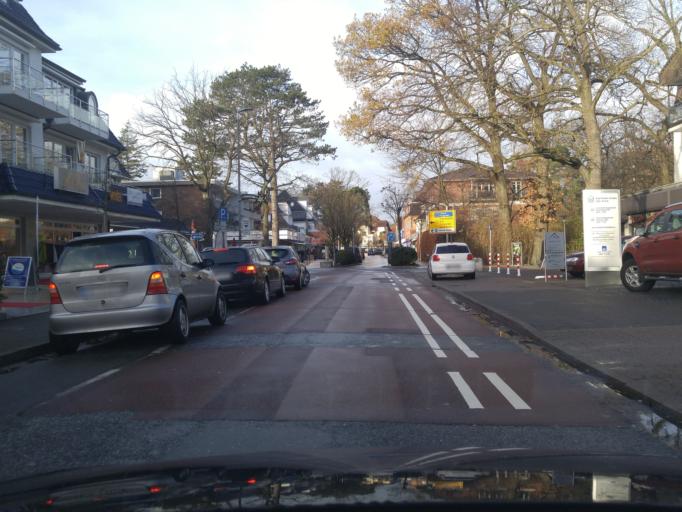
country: DE
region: Schleswig-Holstein
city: Timmendorfer Strand
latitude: 53.9966
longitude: 10.7850
